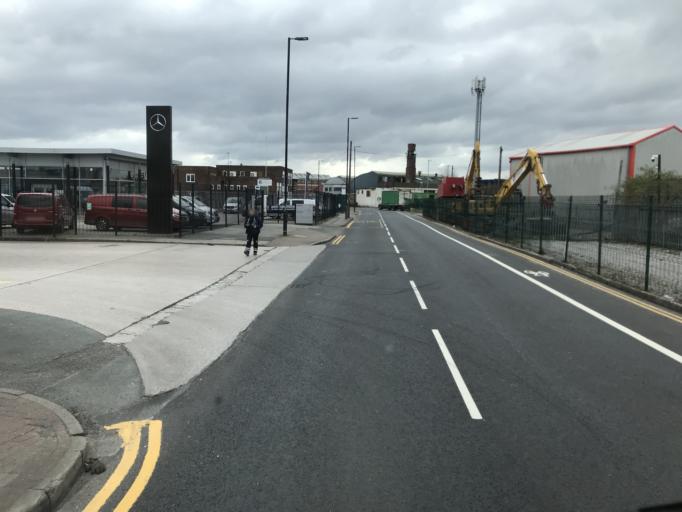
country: GB
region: England
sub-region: Trafford
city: Trafford Park
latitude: 53.4692
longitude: -2.3113
